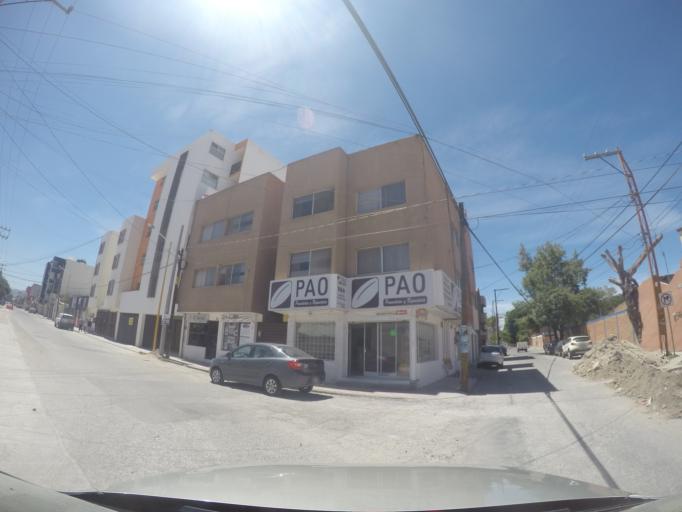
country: MX
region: San Luis Potosi
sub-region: San Luis Potosi
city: San Luis Potosi
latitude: 22.1557
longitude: -100.9949
